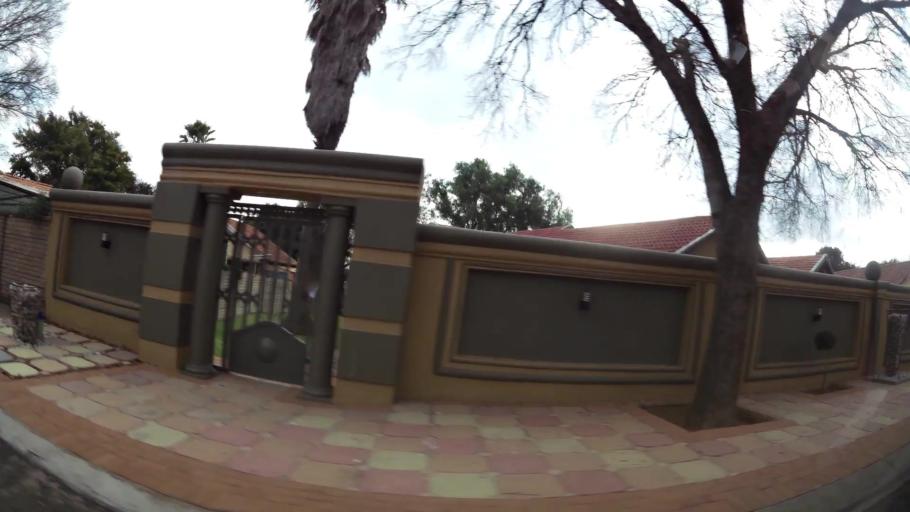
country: ZA
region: Gauteng
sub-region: Ekurhuleni Metropolitan Municipality
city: Benoni
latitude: -26.1319
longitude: 28.3600
